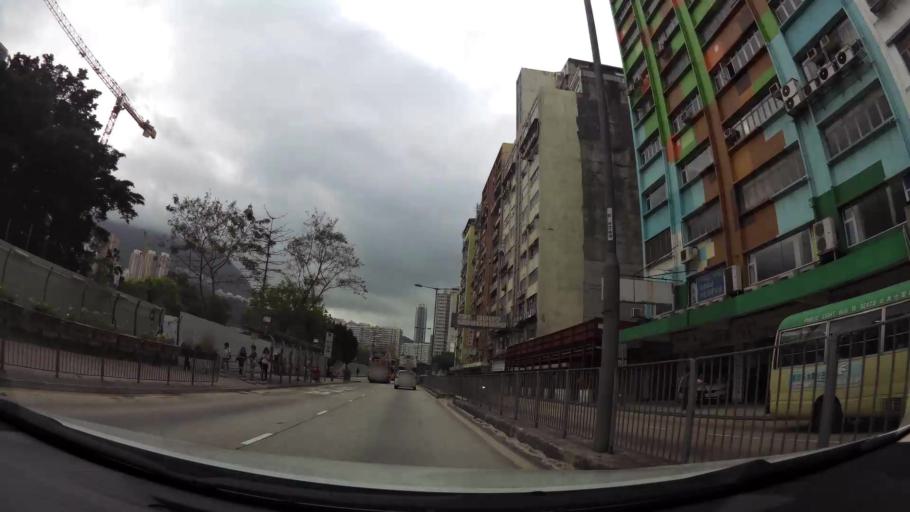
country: HK
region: Wong Tai Sin
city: Wong Tai Sin
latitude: 22.3389
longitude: 114.2000
